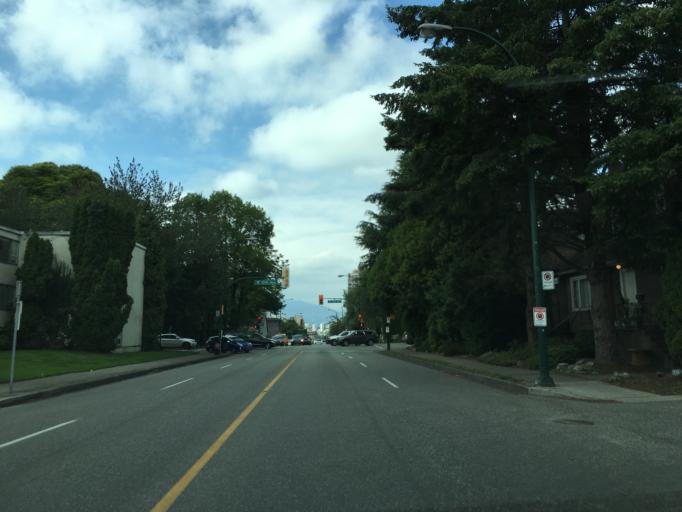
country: CA
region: British Columbia
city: Vancouver
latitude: 49.2602
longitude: -123.1410
